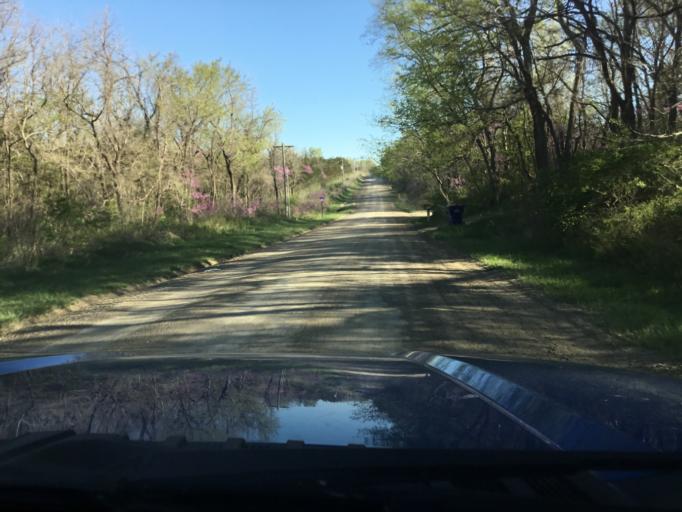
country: US
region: Kansas
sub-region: Douglas County
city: Lawrence
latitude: 38.9606
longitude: -95.3724
